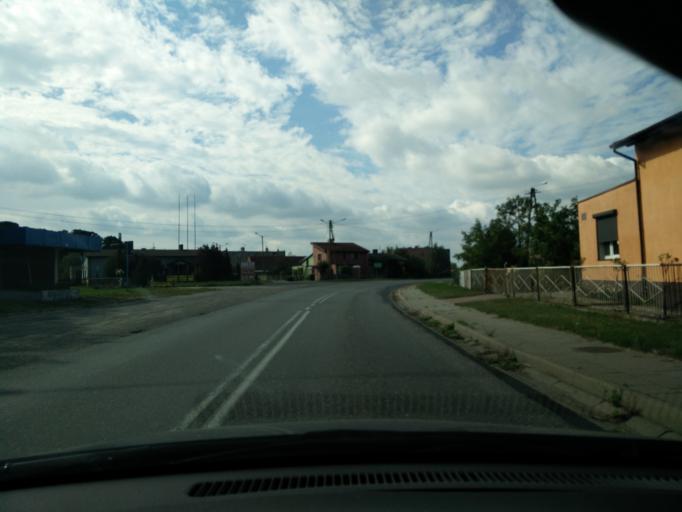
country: PL
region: Greater Poland Voivodeship
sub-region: Powiat sredzki
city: Dominowo
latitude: 52.2501
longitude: 17.3896
